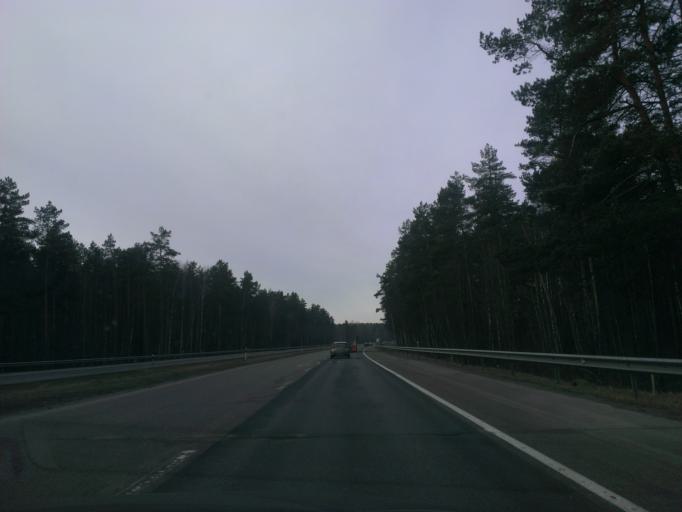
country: LV
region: Garkalne
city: Garkalne
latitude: 57.0500
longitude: 24.4443
